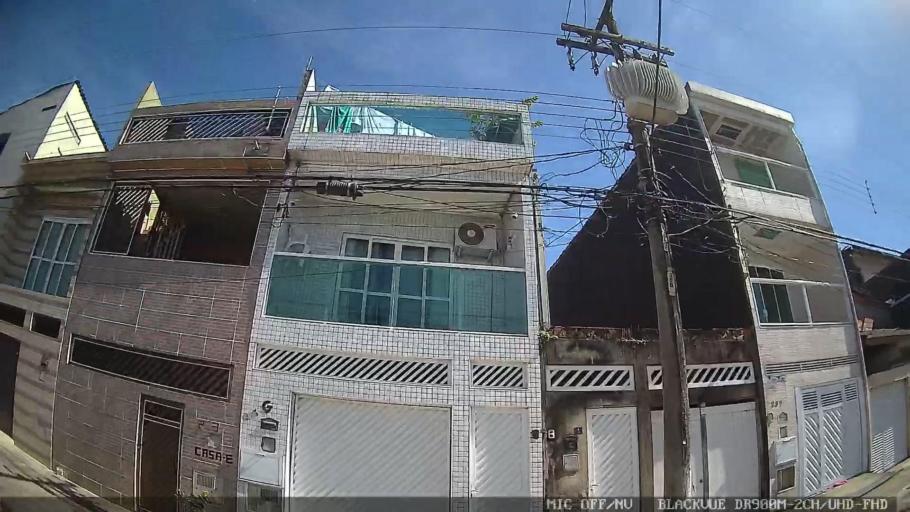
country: BR
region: Sao Paulo
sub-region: Guaruja
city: Guaruja
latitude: -23.9664
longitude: -46.2787
